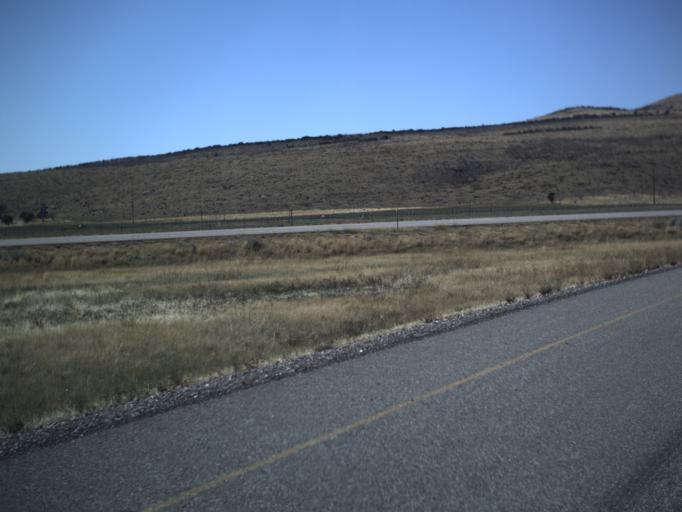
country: US
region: Utah
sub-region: Beaver County
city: Beaver
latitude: 38.5390
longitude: -112.6081
